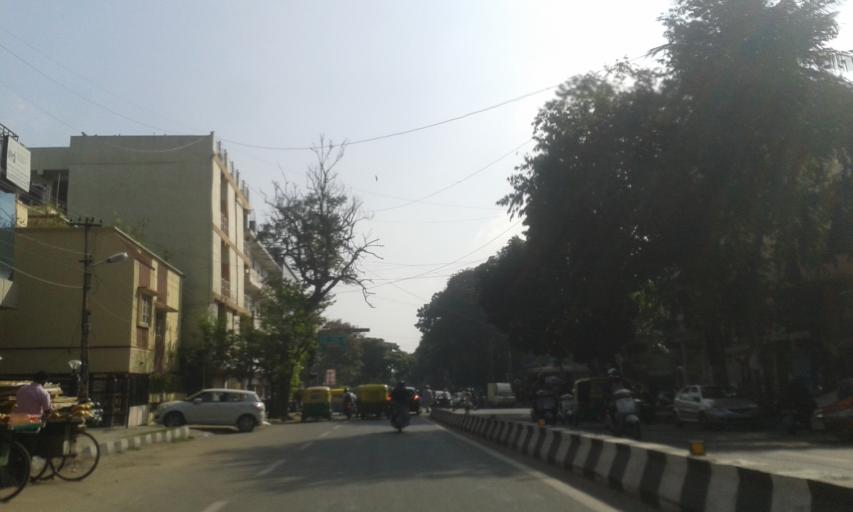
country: IN
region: Karnataka
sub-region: Bangalore Urban
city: Bangalore
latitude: 12.9285
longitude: 77.5966
